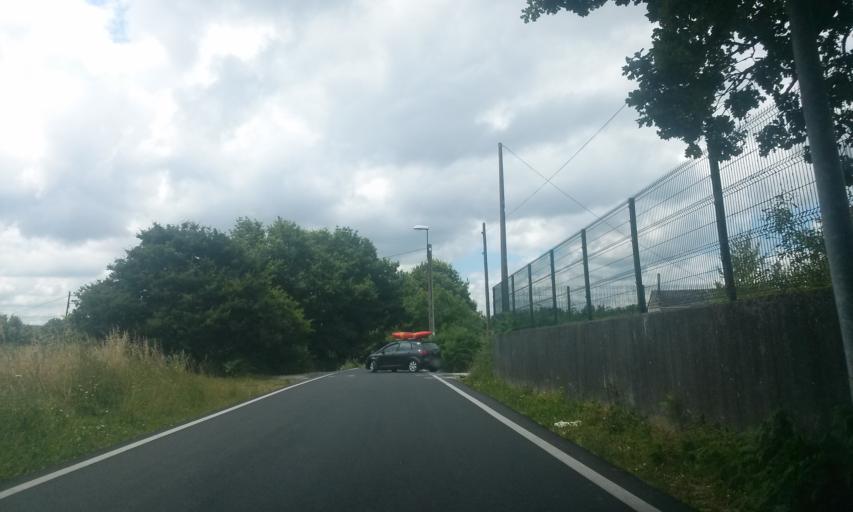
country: ES
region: Galicia
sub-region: Provincia de Lugo
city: Lugo
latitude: 43.0242
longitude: -7.5755
